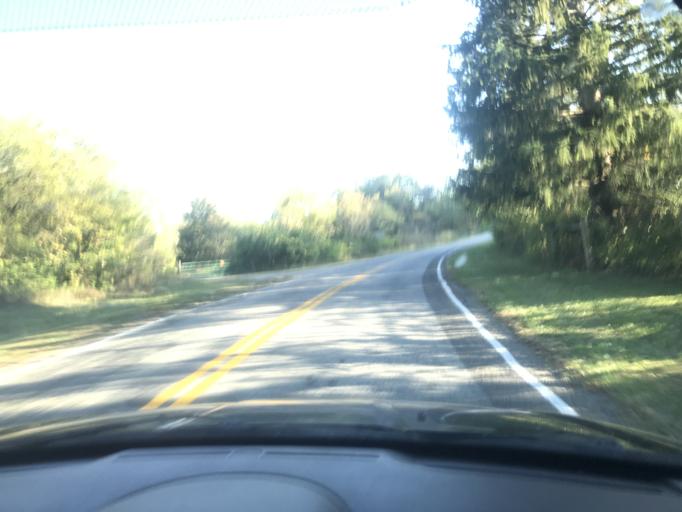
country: US
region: Ohio
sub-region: Logan County
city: De Graff
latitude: 40.2443
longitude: -83.8643
